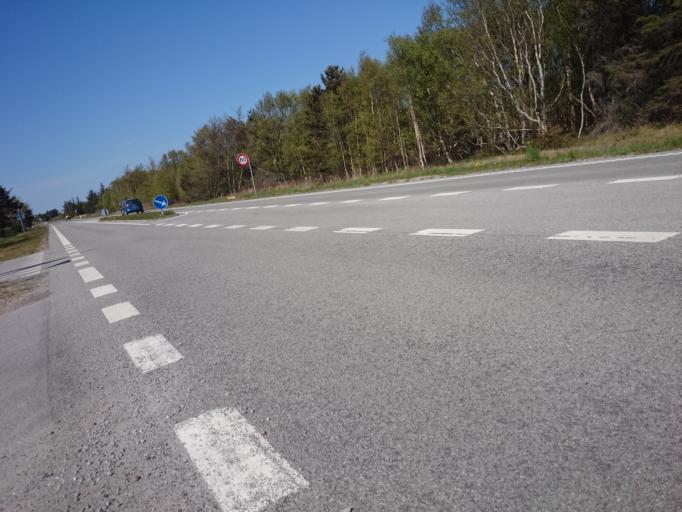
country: DK
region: North Denmark
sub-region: Frederikshavn Kommune
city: Skagen
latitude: 57.7345
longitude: 10.6042
